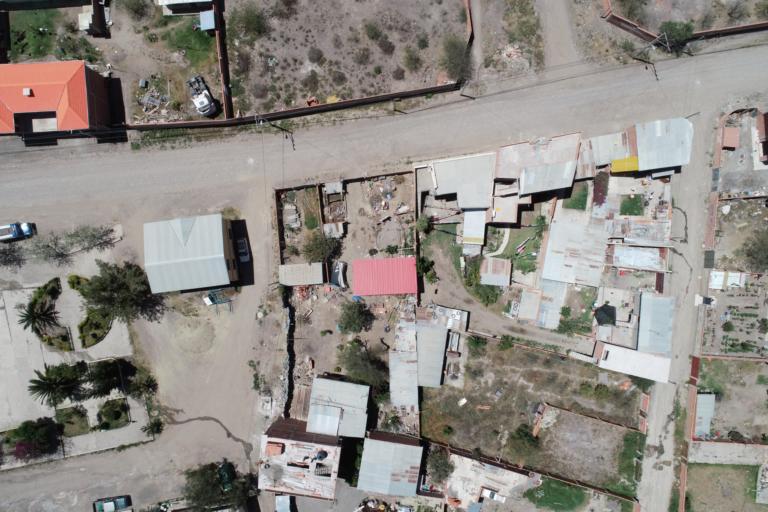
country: BO
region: La Paz
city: La Paz
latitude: -16.6434
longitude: -68.0431
